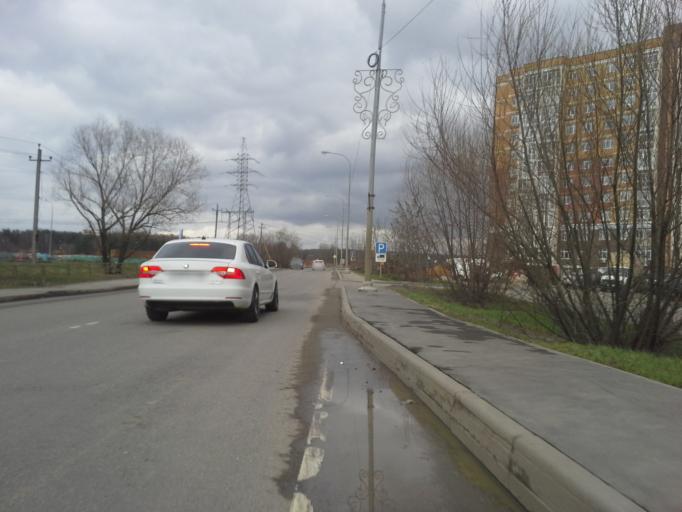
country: RU
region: Moskovskaya
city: Kommunarka
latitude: 55.5726
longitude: 37.4905
